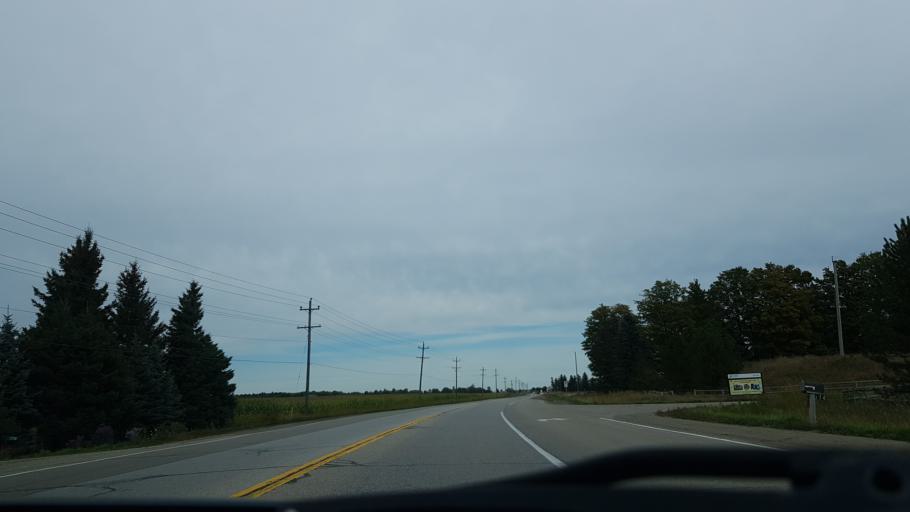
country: CA
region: Ontario
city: Orangeville
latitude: 43.8164
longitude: -80.0440
